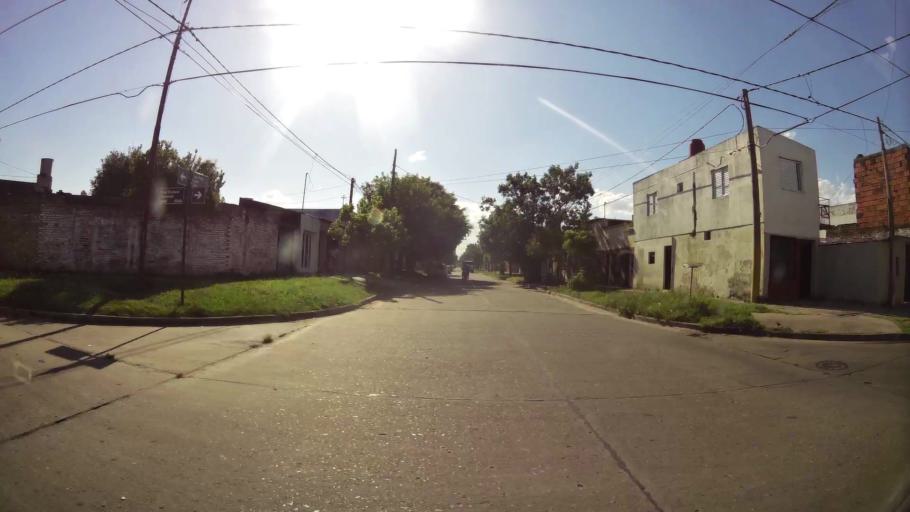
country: AR
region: Santa Fe
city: Santa Fe de la Vera Cruz
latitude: -31.6101
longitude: -60.6864
